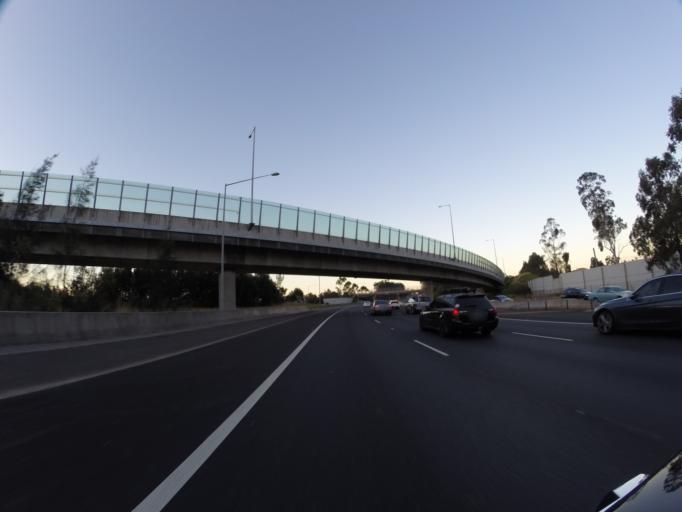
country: AU
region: New South Wales
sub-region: Campbelltown Municipality
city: Glenfield
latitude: -33.9513
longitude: 150.8802
